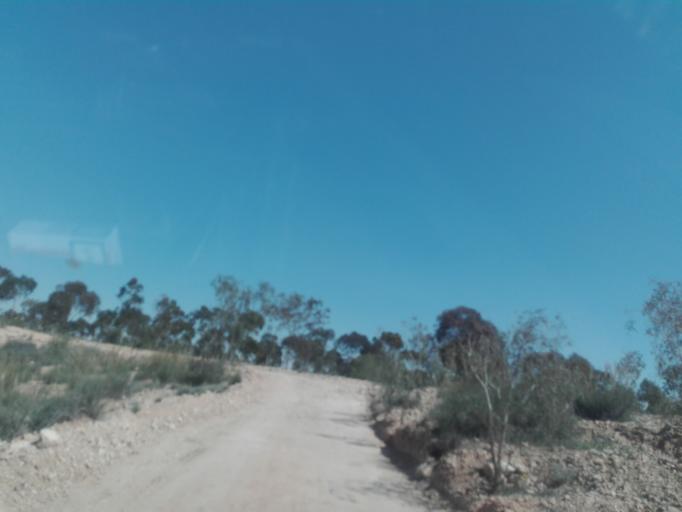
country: TN
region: Safaqis
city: Sfax
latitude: 34.6998
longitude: 10.5307
